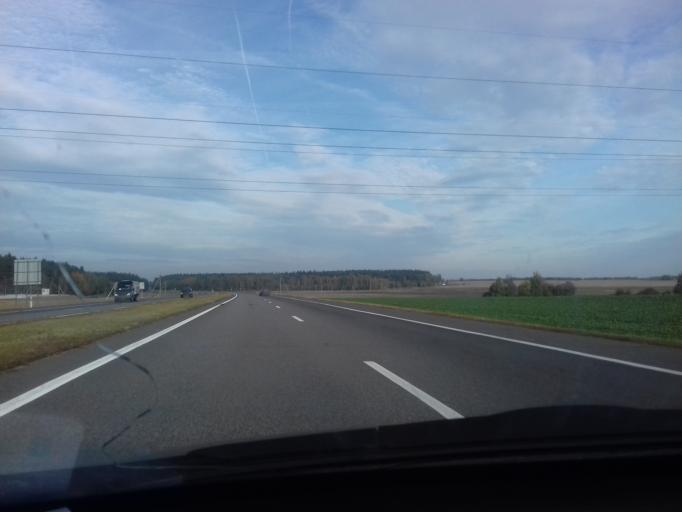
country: BY
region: Minsk
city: Hatava
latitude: 53.7430
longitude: 27.6264
